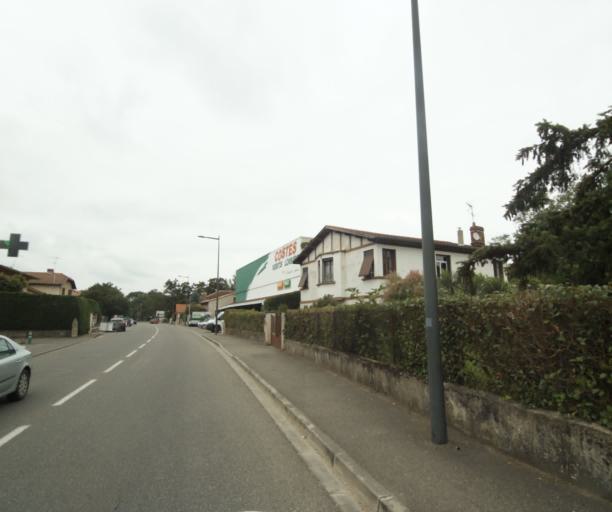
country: FR
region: Midi-Pyrenees
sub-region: Departement du Tarn-et-Garonne
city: Montauban
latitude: 44.0113
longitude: 1.3545
